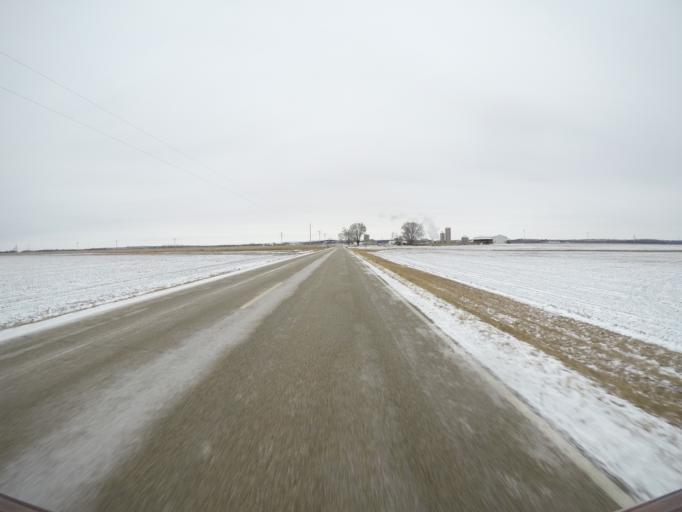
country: US
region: Kansas
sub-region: Pottawatomie County
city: Saint Marys
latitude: 39.2007
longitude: -96.1474
